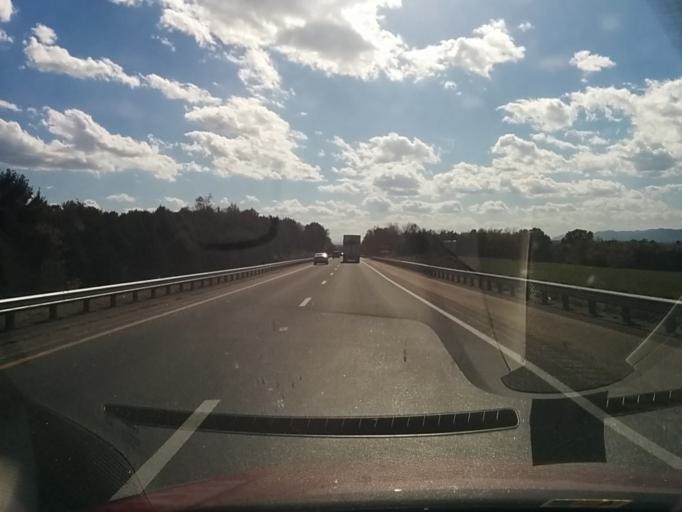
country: US
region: Virginia
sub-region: Rockbridge County
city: East Lexington
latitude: 37.8117
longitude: -79.3865
